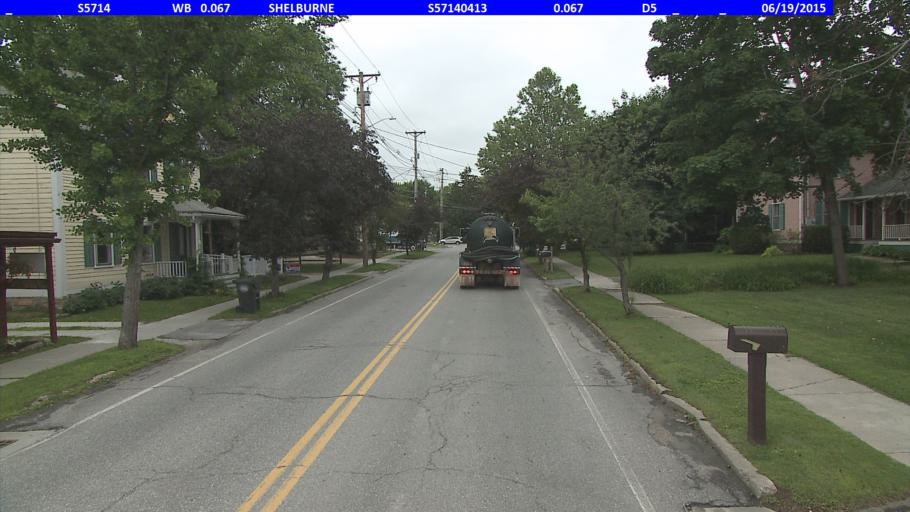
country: US
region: Vermont
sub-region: Chittenden County
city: Burlington
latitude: 44.3809
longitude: -73.2288
